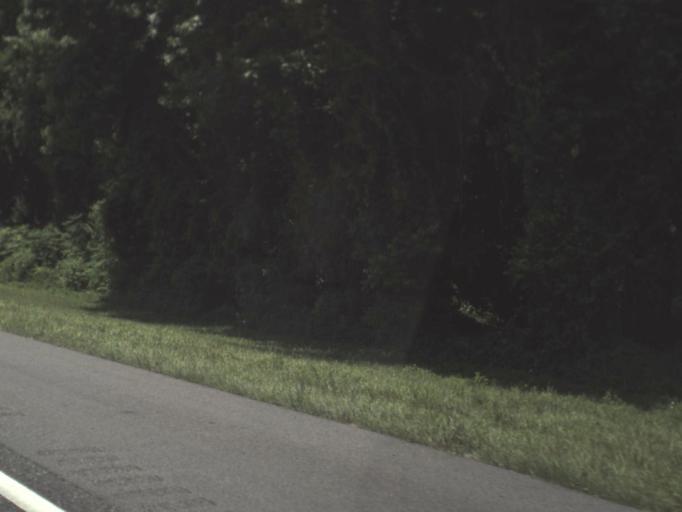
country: US
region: Florida
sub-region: Suwannee County
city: Wellborn
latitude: 30.2708
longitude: -82.7726
